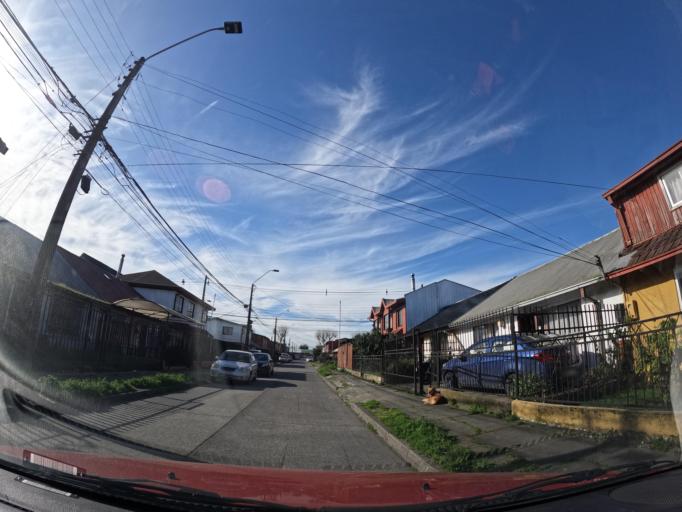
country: CL
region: Biobio
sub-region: Provincia de Concepcion
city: Concepcion
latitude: -36.8083
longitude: -73.0748
